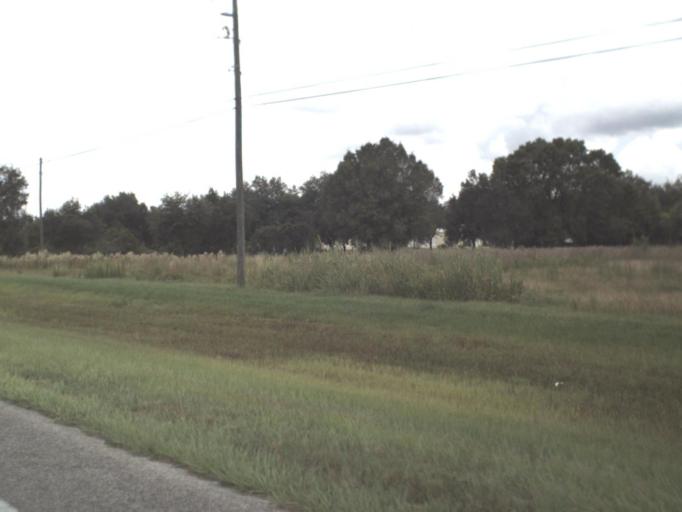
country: US
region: Florida
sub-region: Lee County
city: Alva
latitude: 26.7131
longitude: -81.6549
